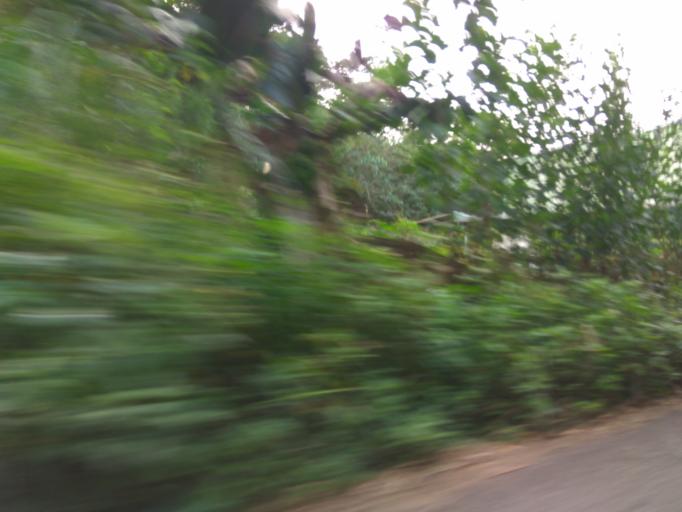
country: TW
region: Taiwan
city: Daxi
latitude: 24.9290
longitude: 121.1890
